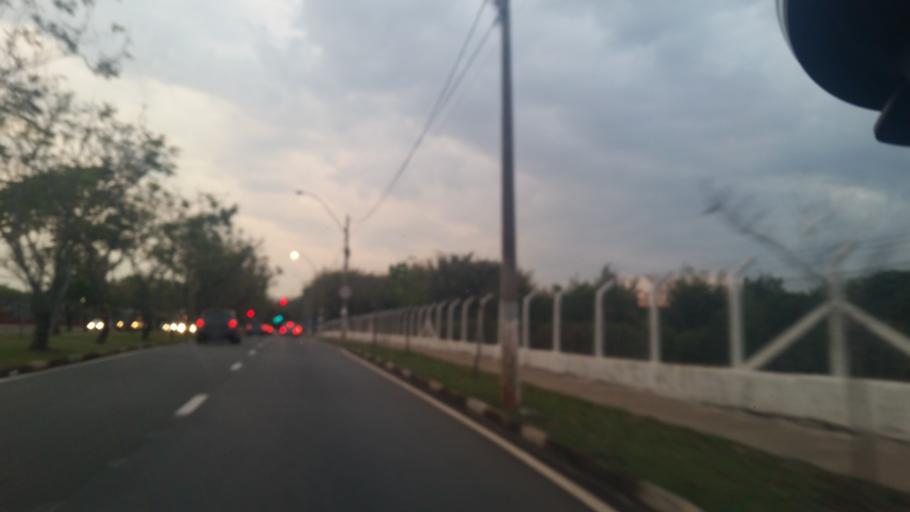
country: BR
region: Sao Paulo
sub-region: Campinas
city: Campinas
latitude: -22.8721
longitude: -47.0664
